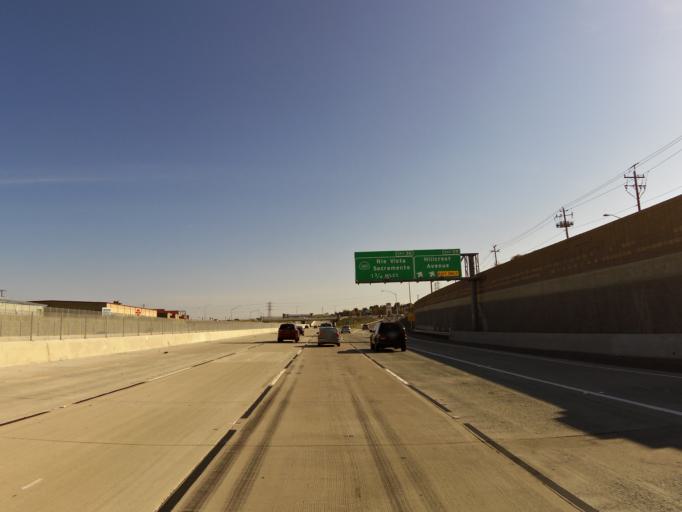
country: US
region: California
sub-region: Contra Costa County
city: Antioch
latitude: 37.9969
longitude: -121.7904
